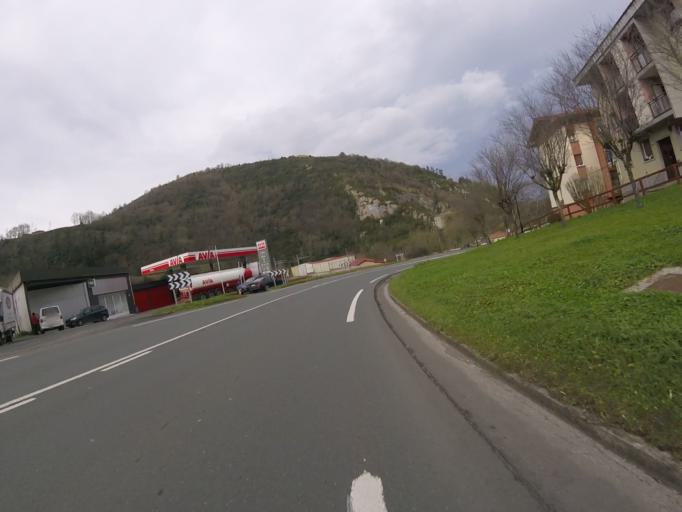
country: ES
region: Basque Country
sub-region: Provincia de Guipuzcoa
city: Cestona
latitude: 43.2413
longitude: -2.2588
